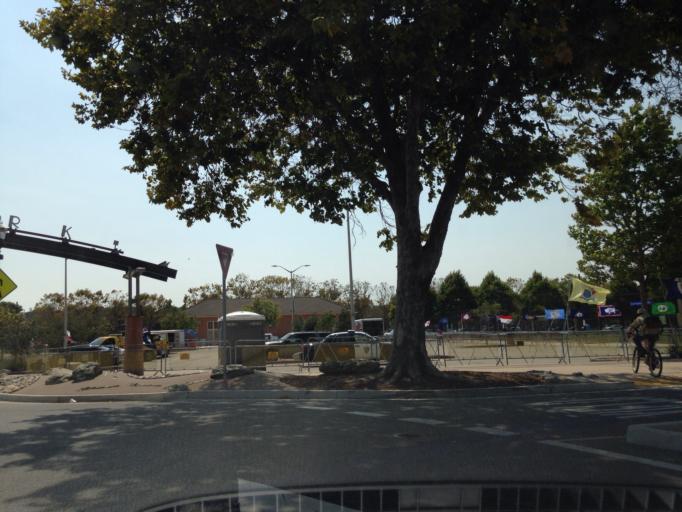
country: US
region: California
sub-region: Santa Cruz County
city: Santa Cruz
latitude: 36.9650
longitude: -122.0263
